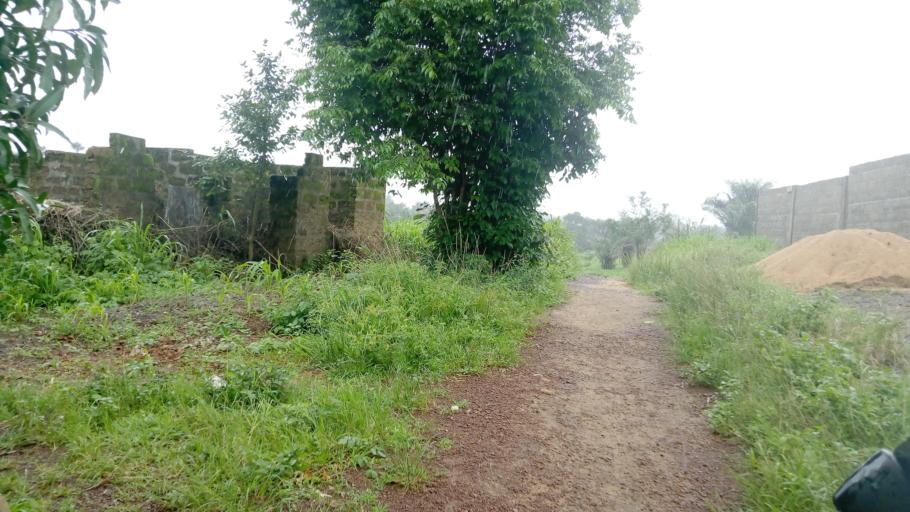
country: SL
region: Southern Province
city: Rotifunk
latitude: 8.4824
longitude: -12.7593
